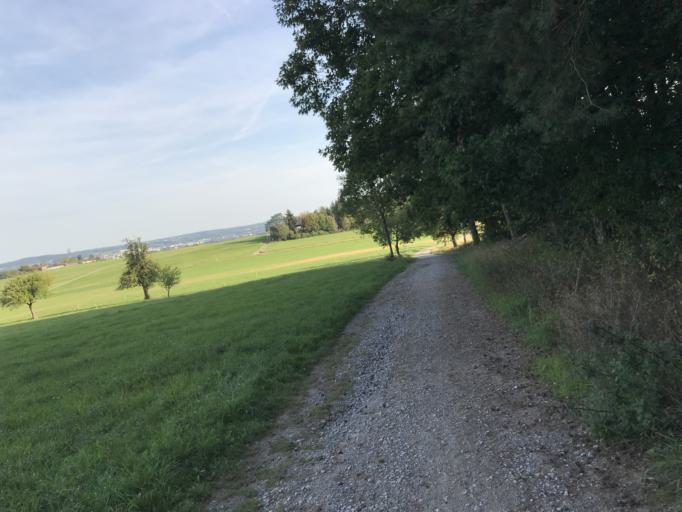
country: DE
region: Hesse
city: Lollar
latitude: 50.6383
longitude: 8.6543
